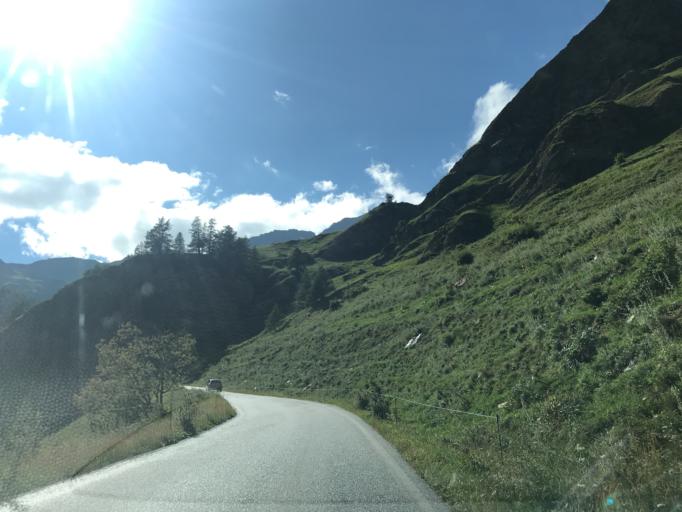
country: IT
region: Piedmont
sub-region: Provincia di Cuneo
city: Pontechianale
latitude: 44.6532
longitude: 6.9894
